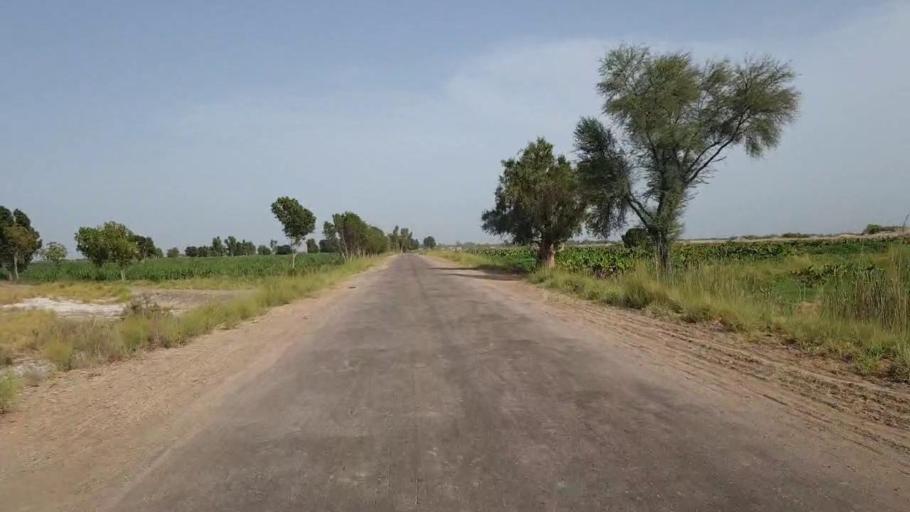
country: PK
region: Sindh
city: Sakrand
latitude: 26.2797
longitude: 68.2689
